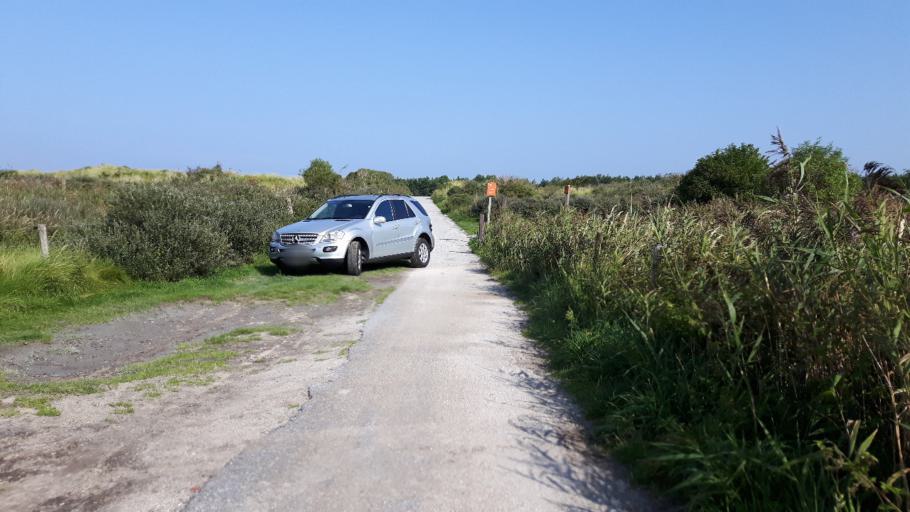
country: NL
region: Friesland
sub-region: Gemeente Ameland
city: Nes
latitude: 53.4570
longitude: 5.8147
